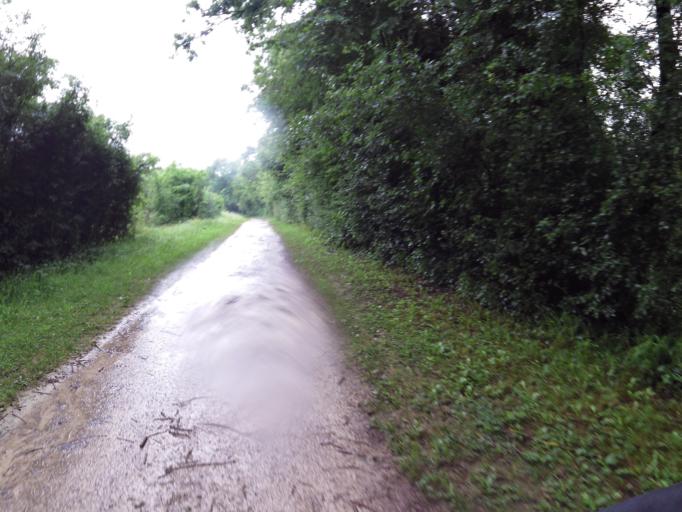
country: FR
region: Poitou-Charentes
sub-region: Departement de la Charente
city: Gond-Pontouvre
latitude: 45.6748
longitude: 0.1539
